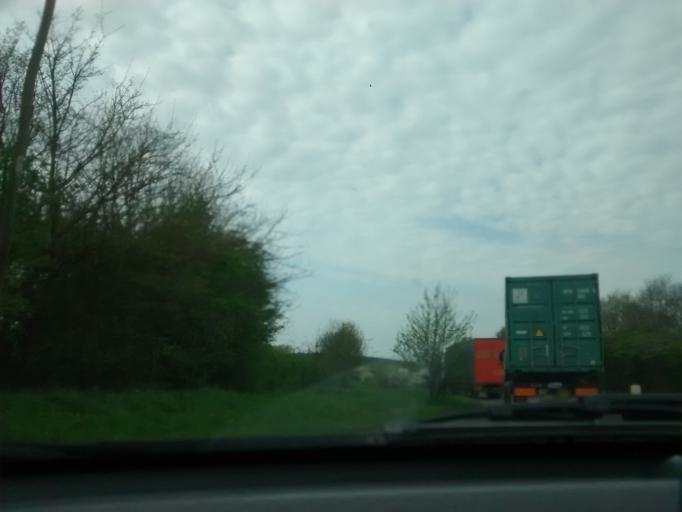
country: GB
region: England
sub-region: Oxfordshire
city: Bicester
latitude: 51.8920
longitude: -1.1290
